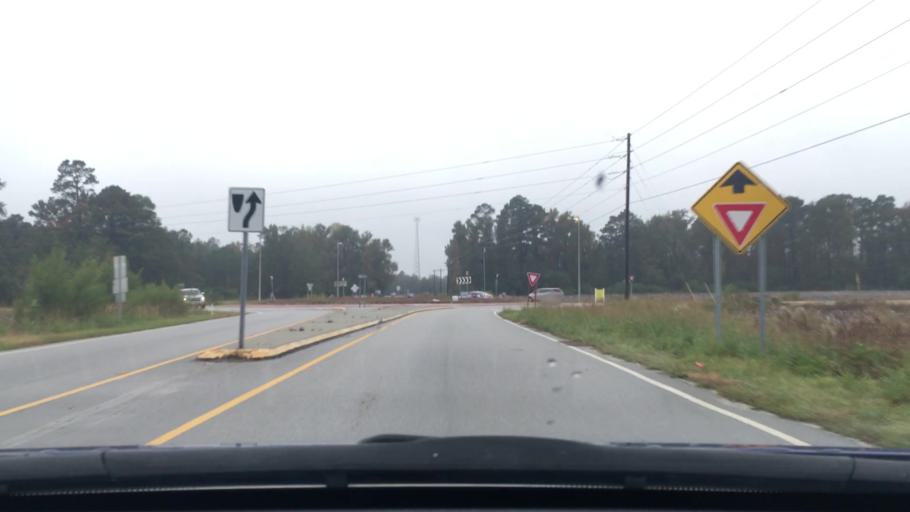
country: US
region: South Carolina
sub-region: Darlington County
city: Darlington
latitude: 34.2511
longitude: -79.9511
